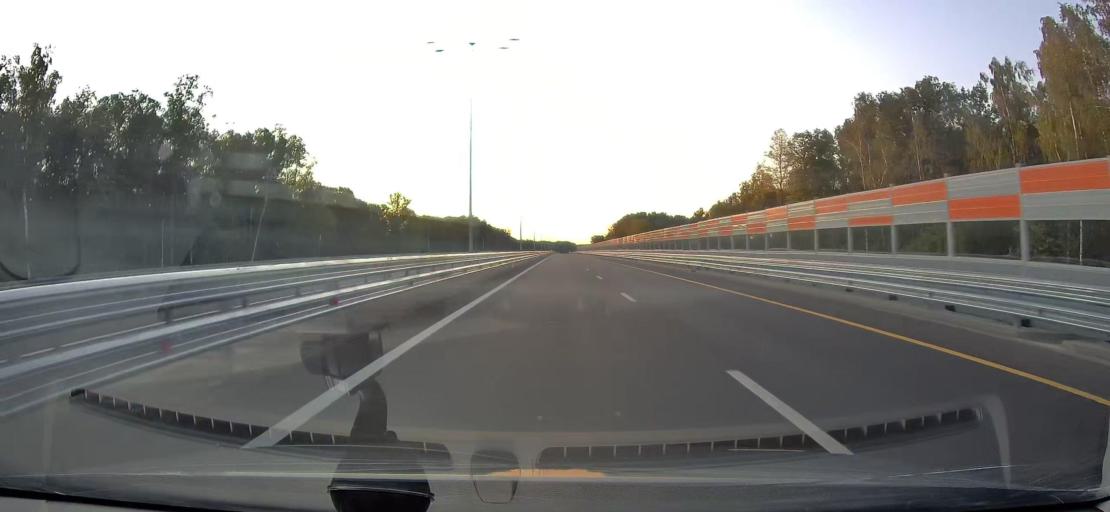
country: RU
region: Moskovskaya
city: L'vovskiy
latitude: 55.3414
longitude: 37.4912
